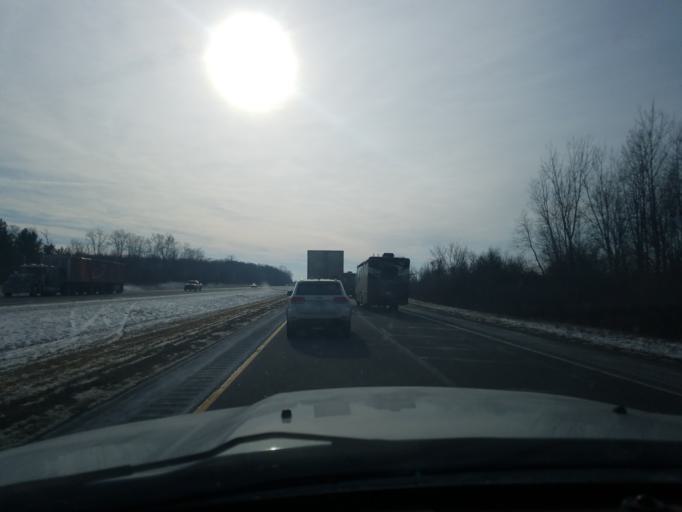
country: US
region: Indiana
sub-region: Huntington County
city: Markle
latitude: 40.8115
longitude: -85.3716
